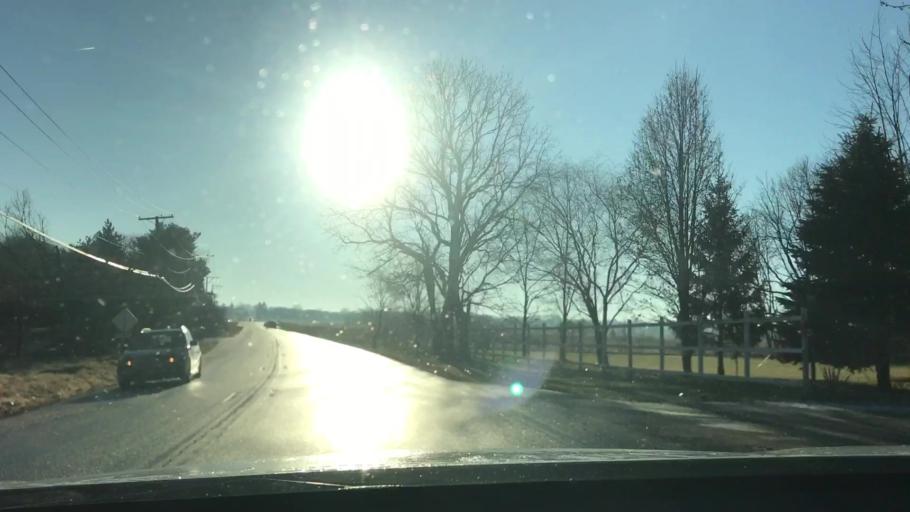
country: US
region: Illinois
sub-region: Kane County
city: Pingree Grove
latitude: 42.0903
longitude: -88.3977
